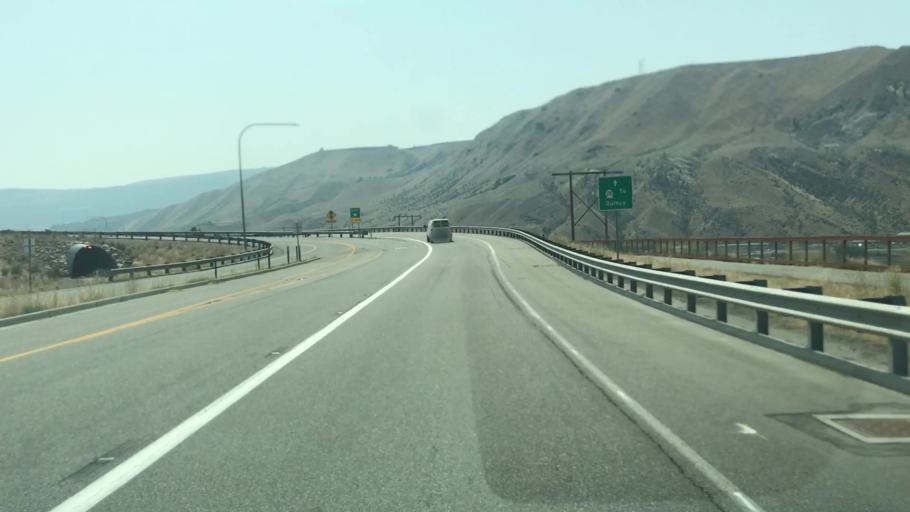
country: US
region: Washington
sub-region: Chelan County
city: South Wenatchee
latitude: 47.4002
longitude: -120.2887
